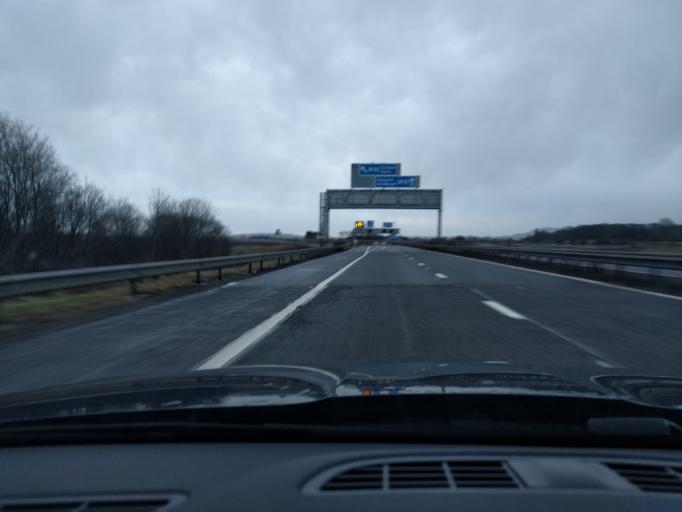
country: GB
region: Scotland
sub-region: Edinburgh
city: Kirkliston
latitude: 55.9569
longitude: -3.4281
